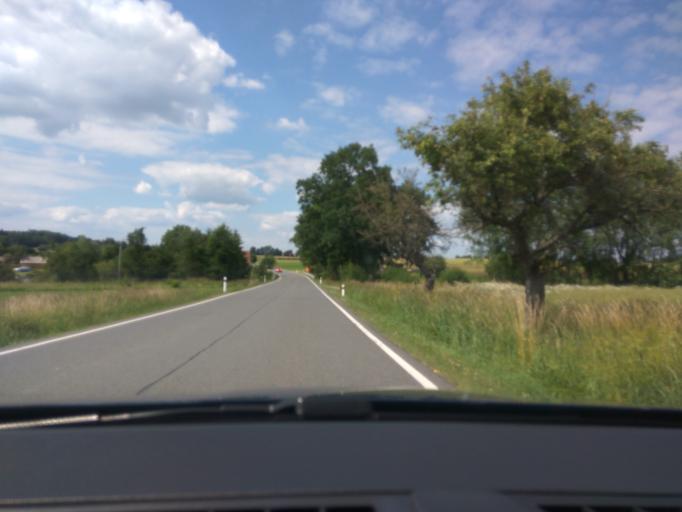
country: CZ
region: Jihocesky
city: Bernartice
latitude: 49.4028
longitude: 14.3631
